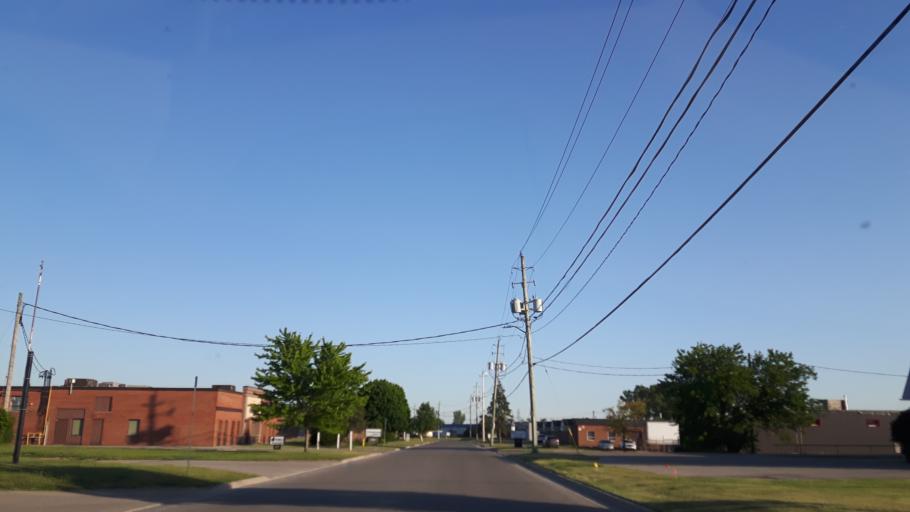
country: CA
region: Ontario
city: London
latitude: 42.9327
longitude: -81.2164
